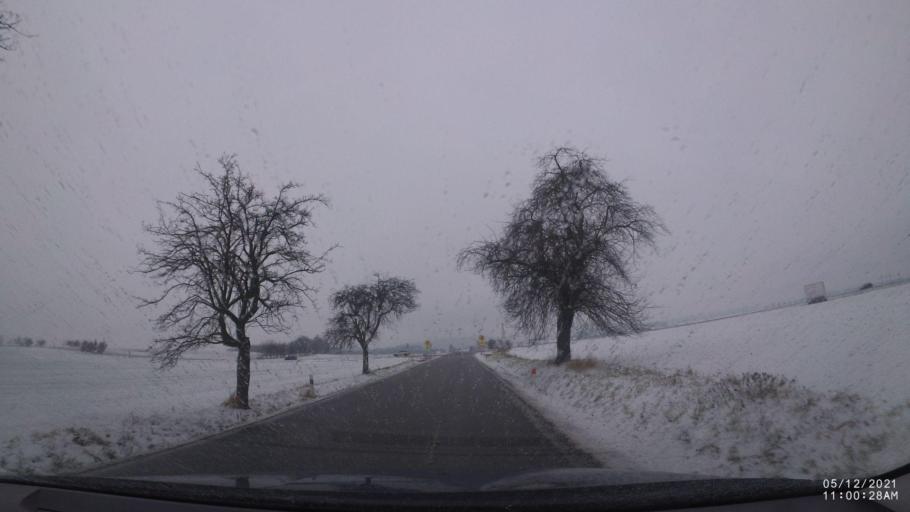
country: CZ
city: Solnice
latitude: 50.1669
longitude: 16.2211
